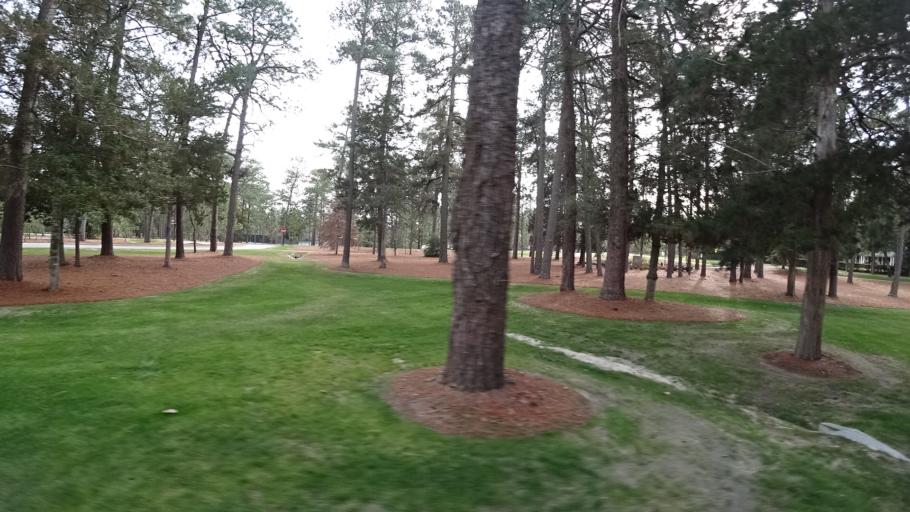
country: US
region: North Carolina
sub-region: Moore County
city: Pinehurst
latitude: 35.1933
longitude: -79.4710
